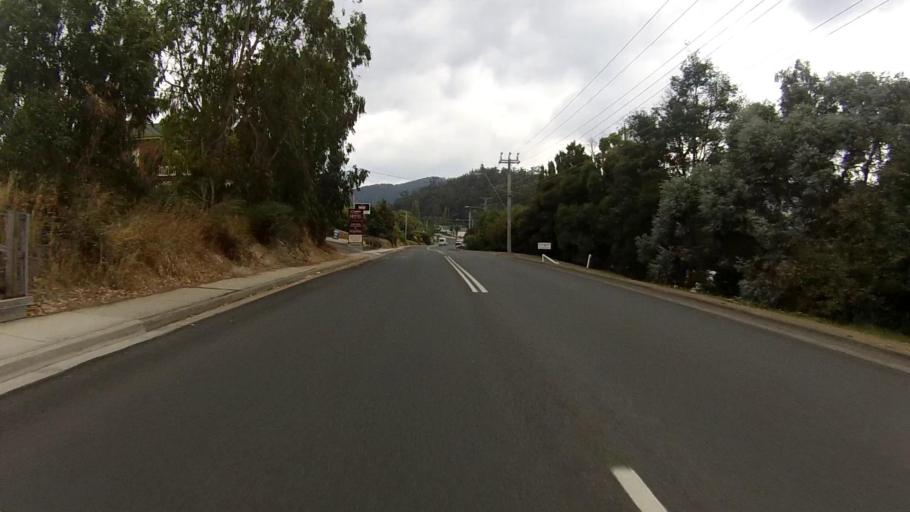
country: AU
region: Tasmania
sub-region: Huon Valley
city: Cygnet
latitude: -43.1572
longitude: 147.0744
